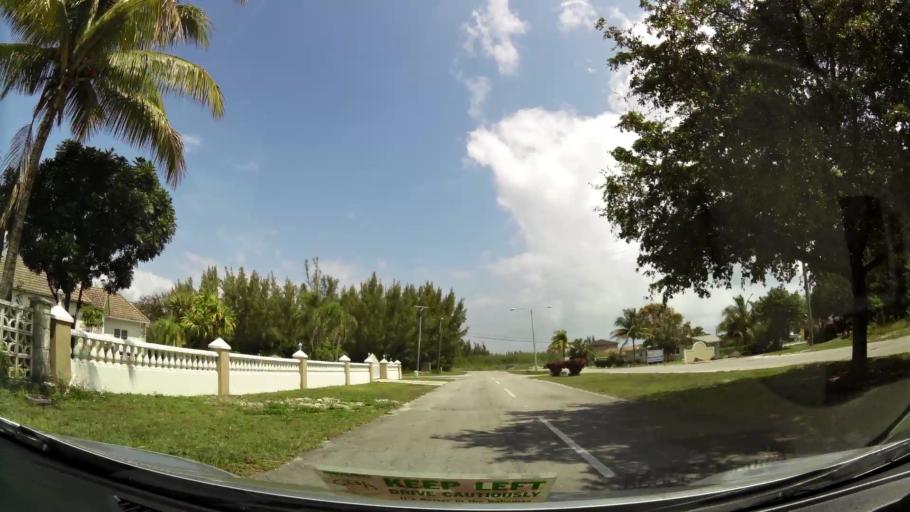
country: BS
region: Freeport
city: Lucaya
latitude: 26.5214
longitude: -78.6207
